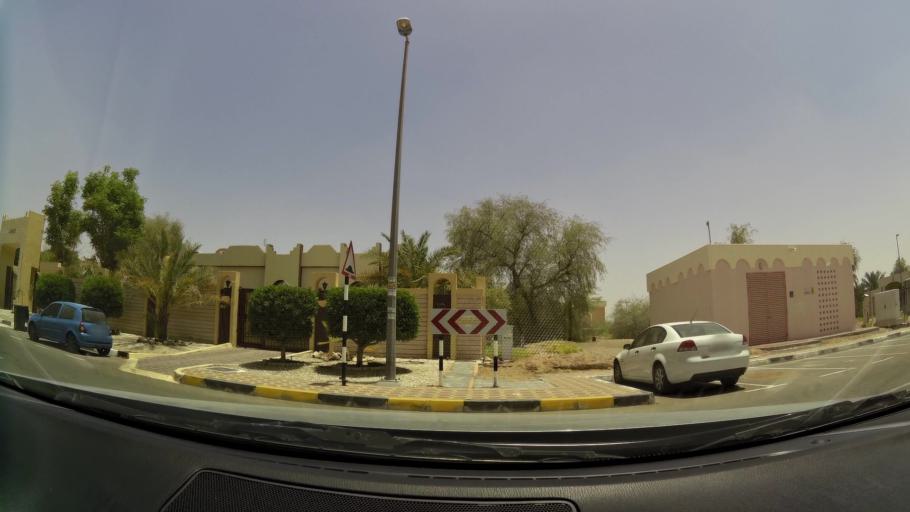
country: OM
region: Al Buraimi
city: Al Buraymi
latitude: 24.2669
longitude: 55.7166
